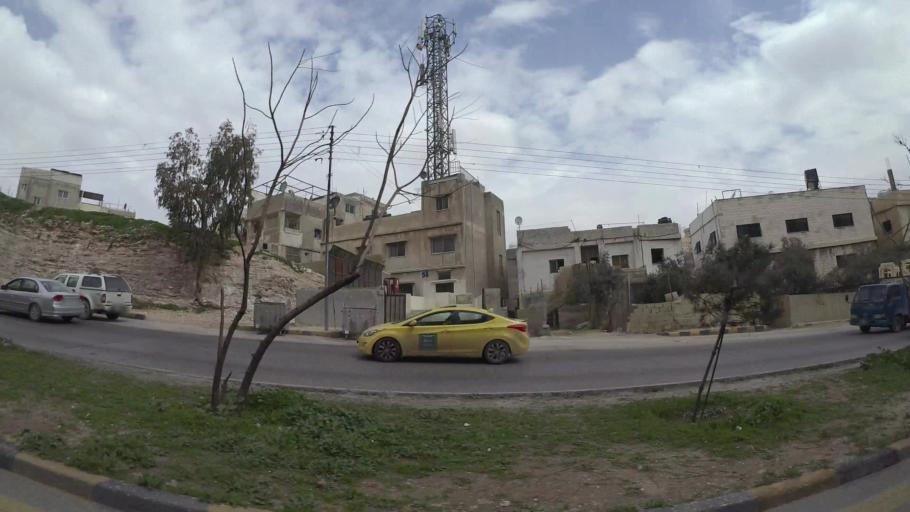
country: JO
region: Amman
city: Amman
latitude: 31.9672
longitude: 35.9497
